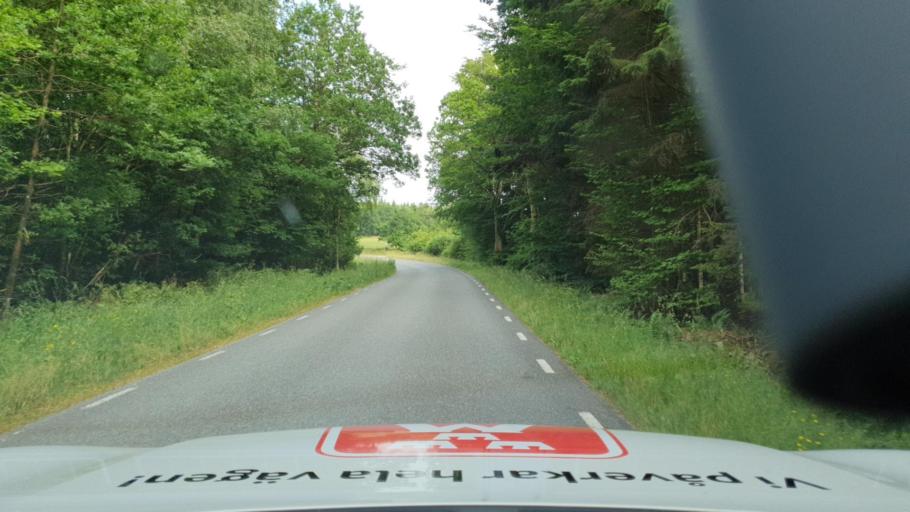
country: SE
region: Skane
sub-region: Kristianstads Kommun
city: Degeberga
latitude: 55.6938
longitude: 14.0667
